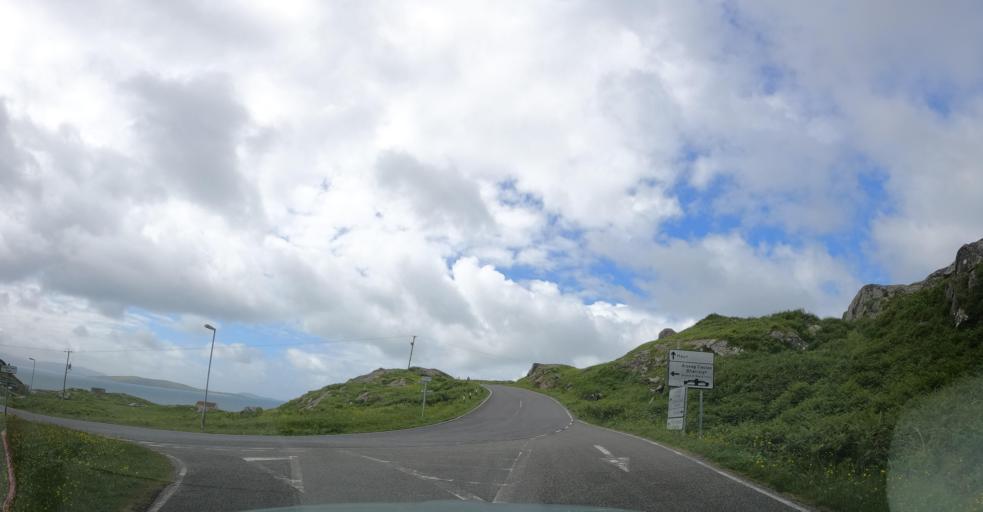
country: GB
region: Scotland
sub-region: Eilean Siar
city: Isle of South Uist
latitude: 57.0739
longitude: -7.3006
